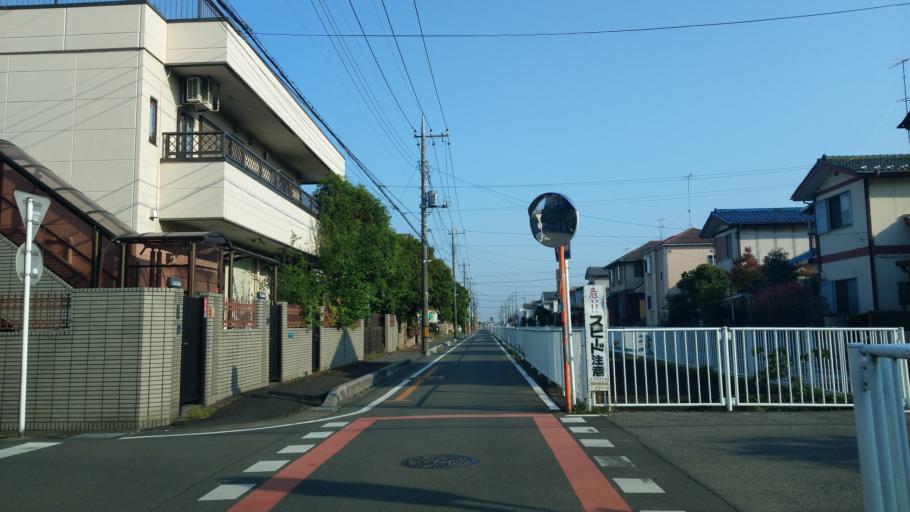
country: JP
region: Saitama
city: Yono
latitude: 35.8907
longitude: 139.5785
